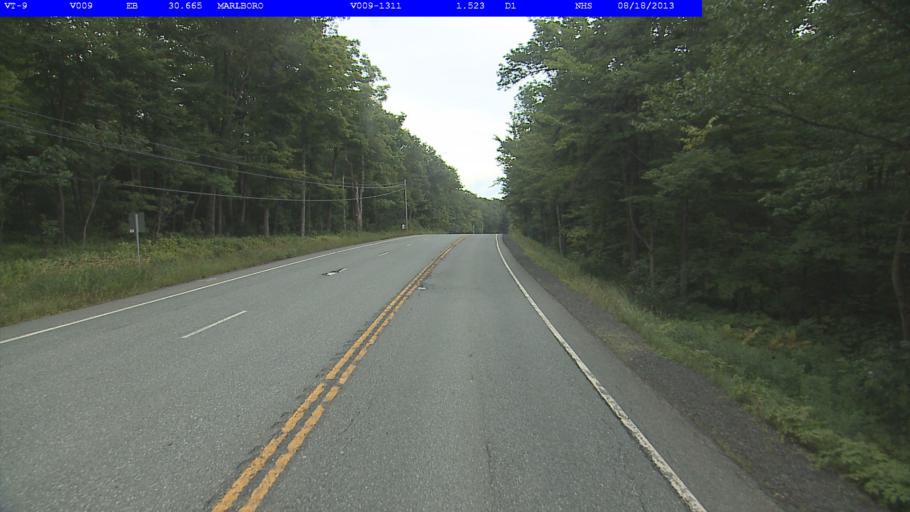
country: US
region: Vermont
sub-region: Windham County
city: Dover
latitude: 42.8628
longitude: -72.7847
